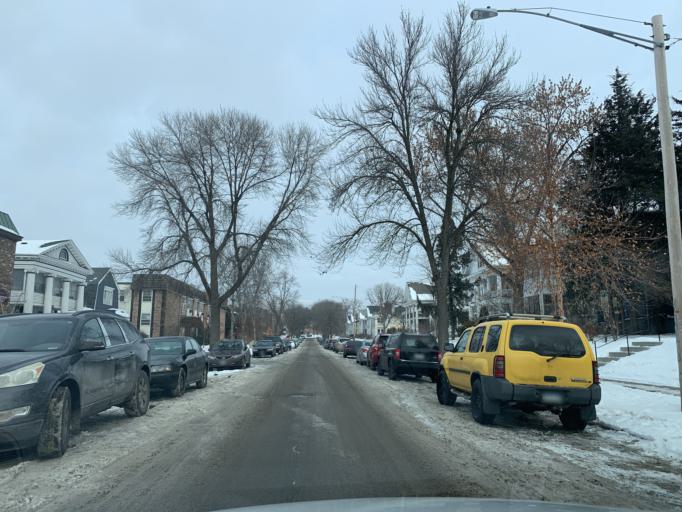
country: US
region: Minnesota
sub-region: Hennepin County
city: Minneapolis
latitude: 44.9596
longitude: -93.2829
